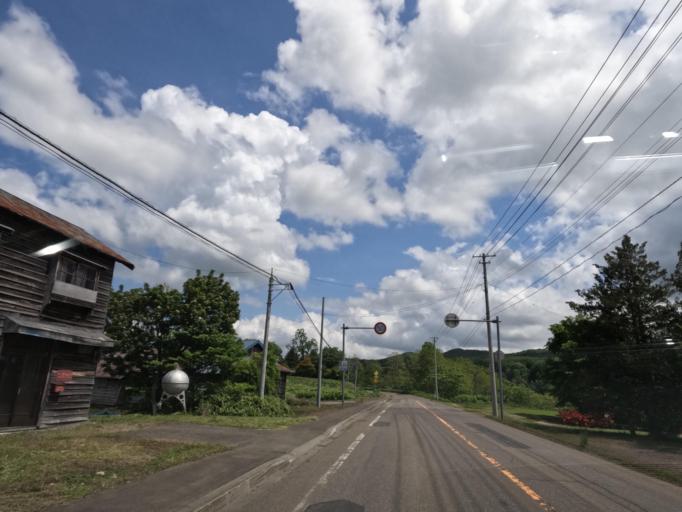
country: JP
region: Hokkaido
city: Takikawa
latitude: 43.5846
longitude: 141.7876
